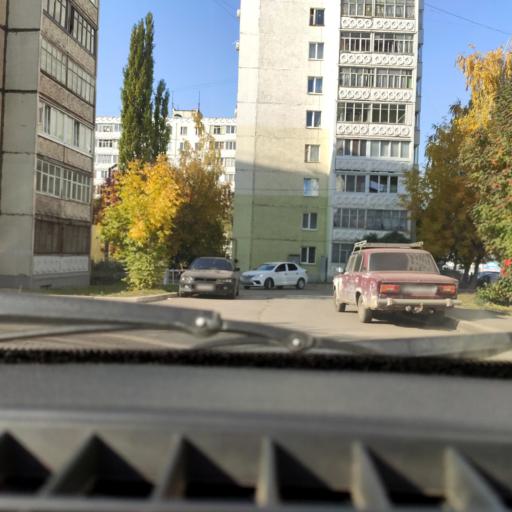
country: RU
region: Bashkortostan
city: Ufa
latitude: 54.7227
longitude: 55.9935
